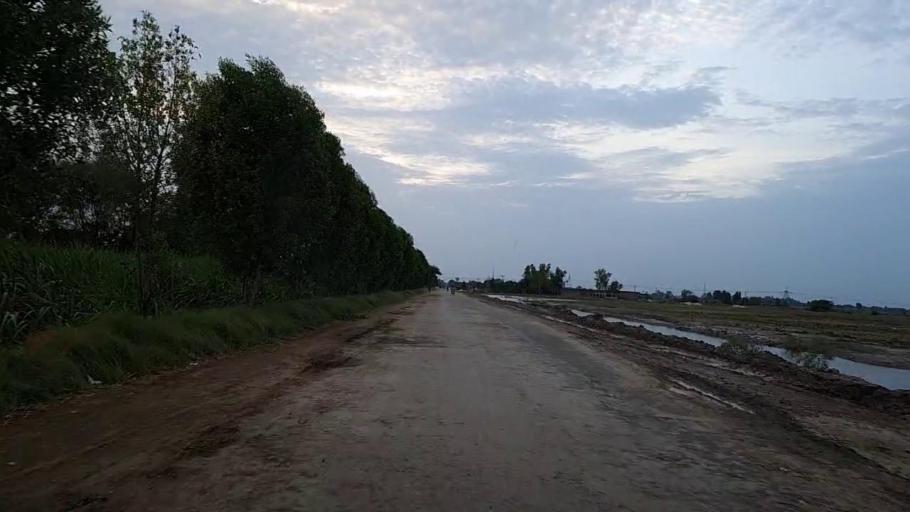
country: PK
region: Sindh
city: Naushahro Firoz
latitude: 26.8272
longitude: 68.1495
